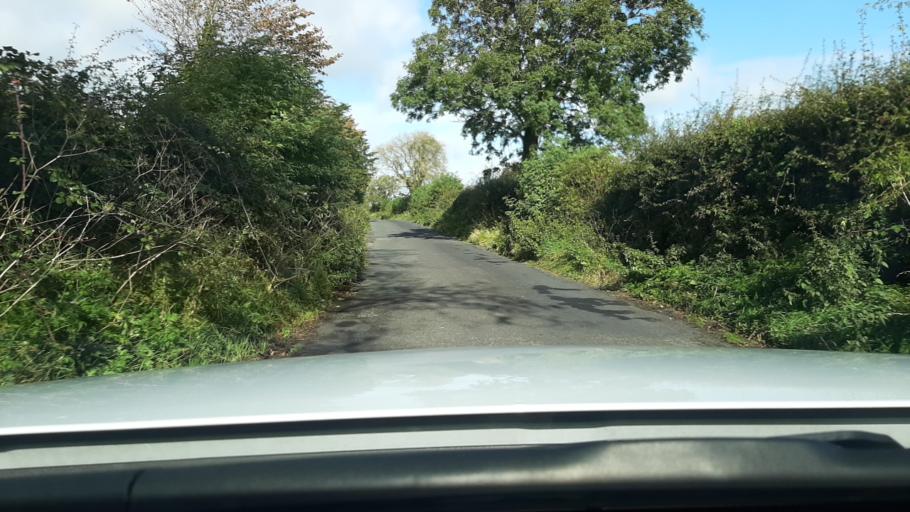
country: IE
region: Leinster
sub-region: Kildare
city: Kildare
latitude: 53.1726
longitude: -6.9216
